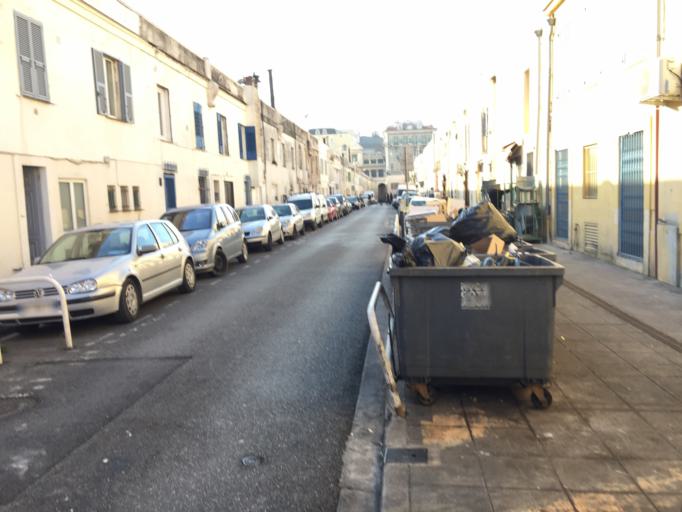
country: FR
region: Provence-Alpes-Cote d'Azur
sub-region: Departement des Alpes-Maritimes
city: Nice
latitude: 43.6953
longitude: 7.2759
